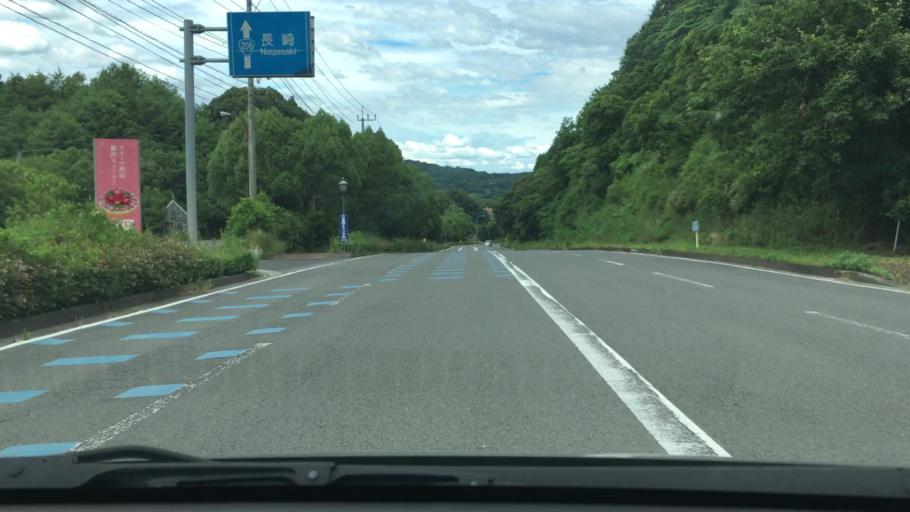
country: JP
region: Nagasaki
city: Sasebo
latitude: 32.9925
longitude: 129.7508
